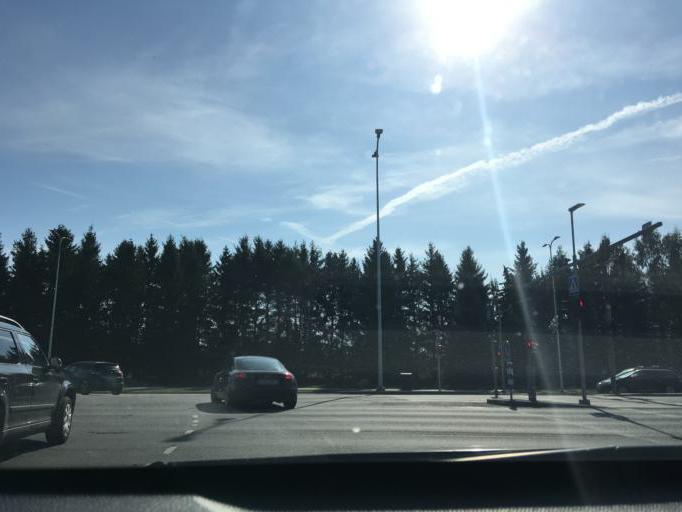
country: EE
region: Harju
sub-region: Saue vald
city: Laagri
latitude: 59.4261
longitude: 24.6565
